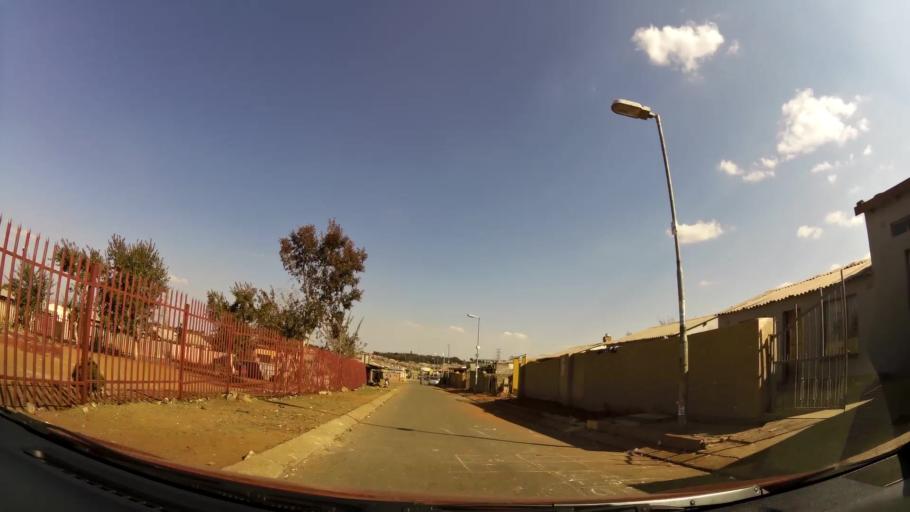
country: ZA
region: Gauteng
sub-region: City of Johannesburg Metropolitan Municipality
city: Soweto
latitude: -26.2348
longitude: 27.8758
